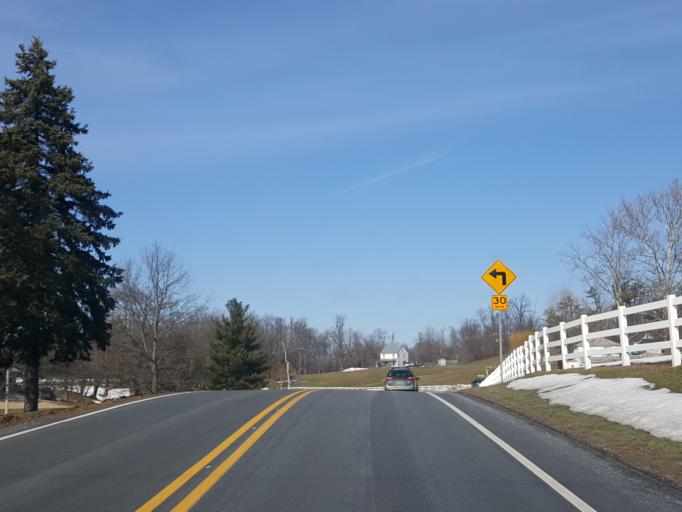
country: US
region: Pennsylvania
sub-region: Lebanon County
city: Campbelltown
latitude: 40.2664
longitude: -76.5579
